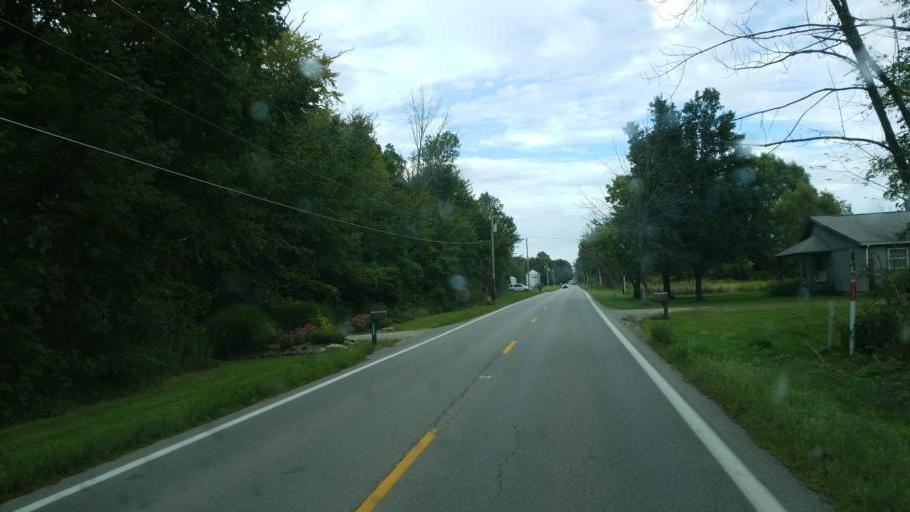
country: US
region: Ohio
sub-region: Franklin County
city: New Albany
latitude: 40.1514
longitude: -82.8084
